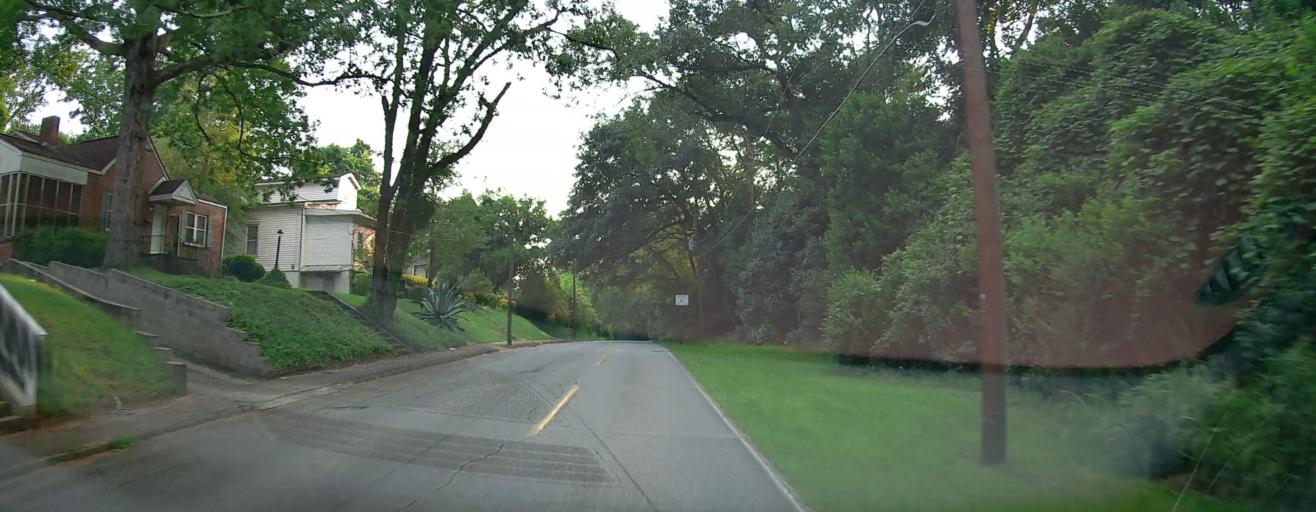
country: US
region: Georgia
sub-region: Bibb County
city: Macon
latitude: 32.8577
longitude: -83.6245
